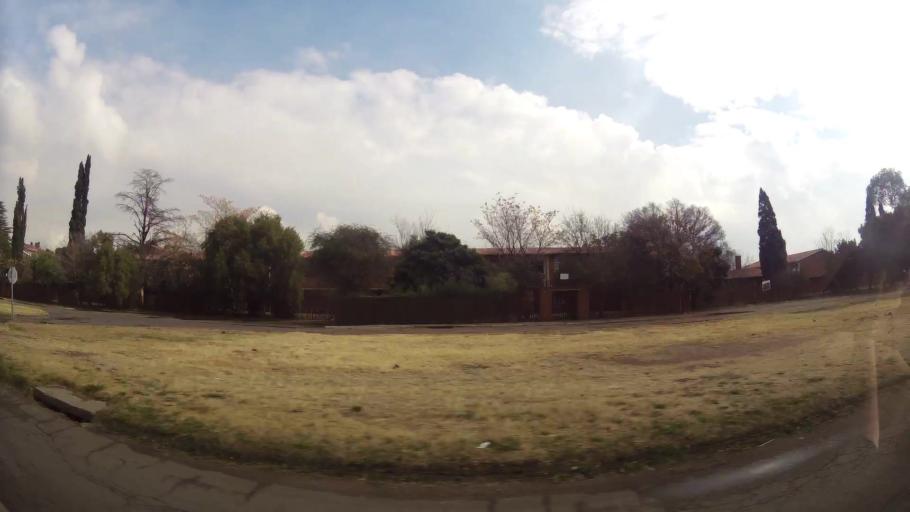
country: ZA
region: Gauteng
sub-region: Sedibeng District Municipality
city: Vereeniging
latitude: -26.6726
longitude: 27.9189
